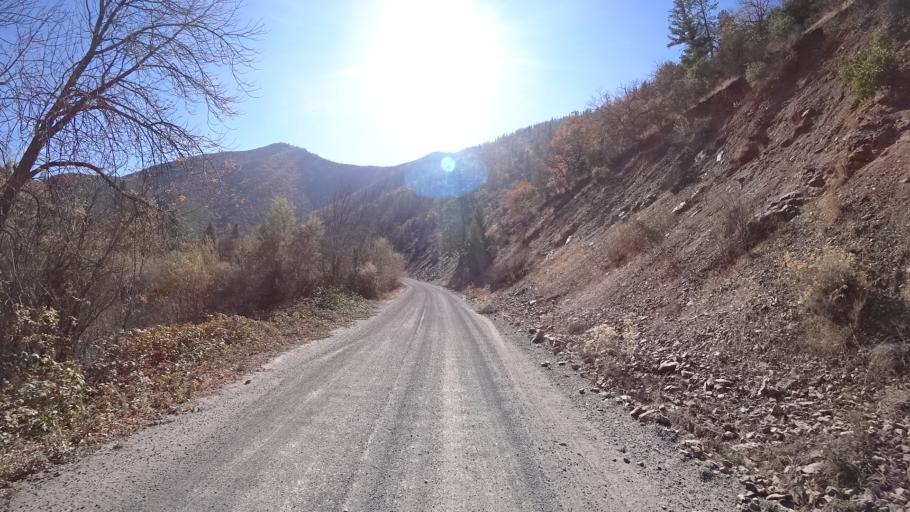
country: US
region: California
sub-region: Siskiyou County
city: Yreka
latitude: 41.8292
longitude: -122.6620
